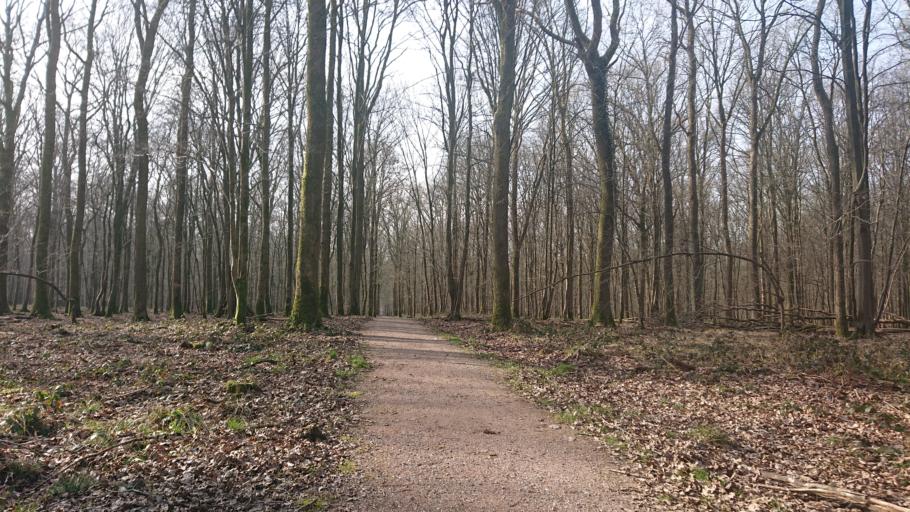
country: FR
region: Nord-Pas-de-Calais
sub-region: Departement du Nord
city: Maroilles
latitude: 50.1712
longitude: 3.7277
